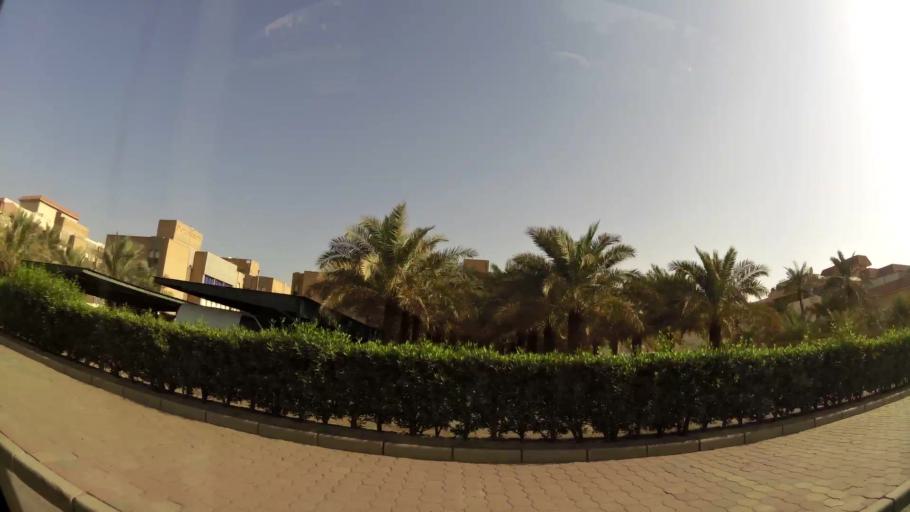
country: KW
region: Muhafazat Hawalli
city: Ar Rumaythiyah
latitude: 29.3074
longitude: 48.0669
